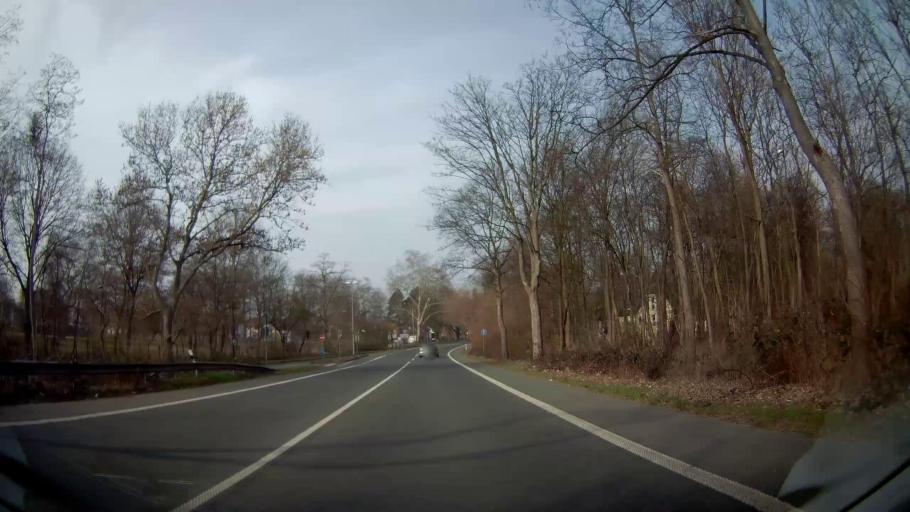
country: DE
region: North Rhine-Westphalia
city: Meiderich
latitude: 51.4614
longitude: 6.7000
